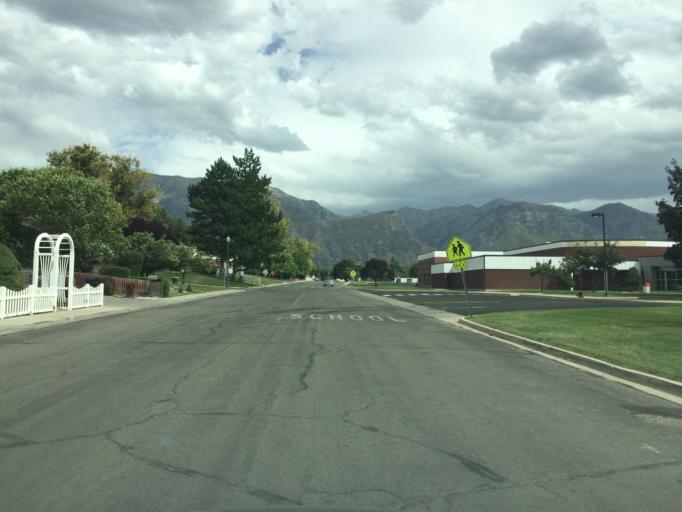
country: US
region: Utah
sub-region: Utah County
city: Orem
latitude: 40.2806
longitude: -111.7042
